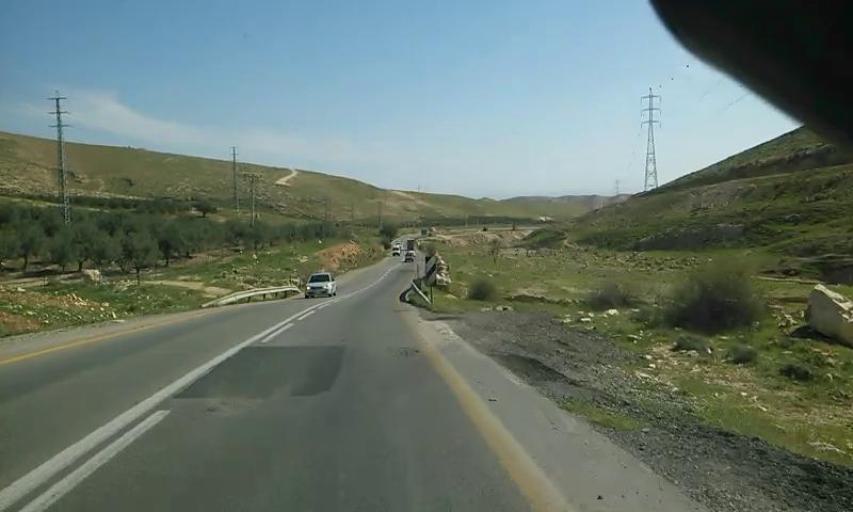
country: PS
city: Az Za`ayyim
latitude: 31.8079
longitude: 35.3160
